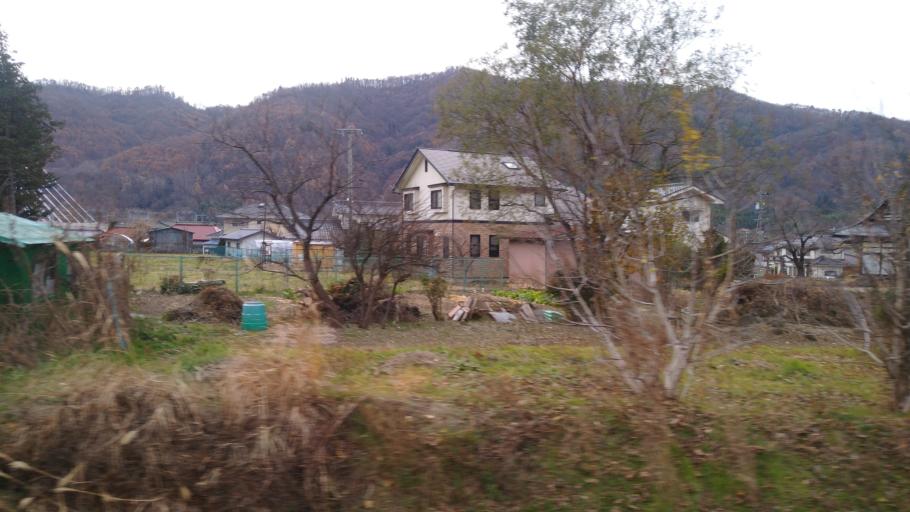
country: JP
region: Nagano
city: Ueda
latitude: 36.3812
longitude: 138.2685
